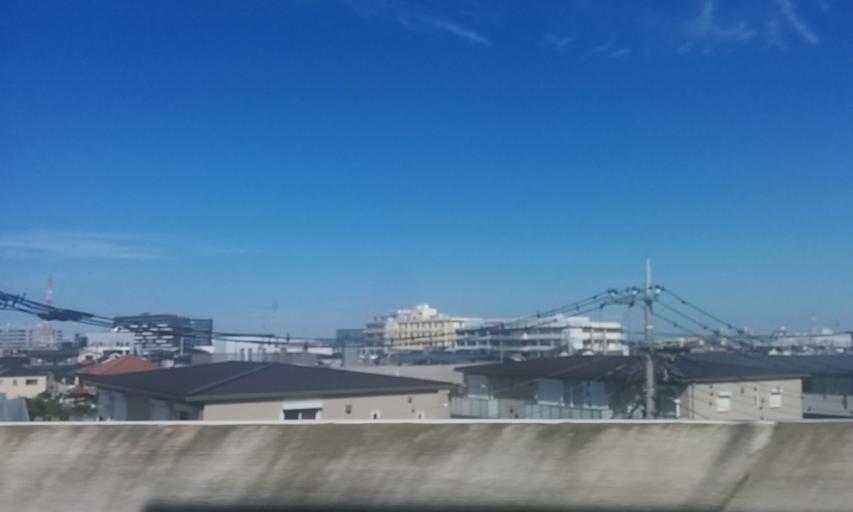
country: JP
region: Chiba
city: Nagareyama
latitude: 35.8286
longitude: 139.8811
